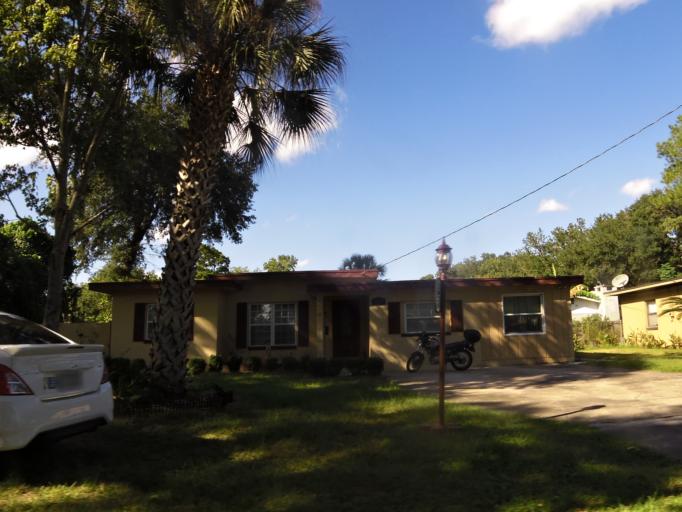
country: US
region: Florida
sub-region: Duval County
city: Jacksonville
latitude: 30.2630
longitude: -81.6347
